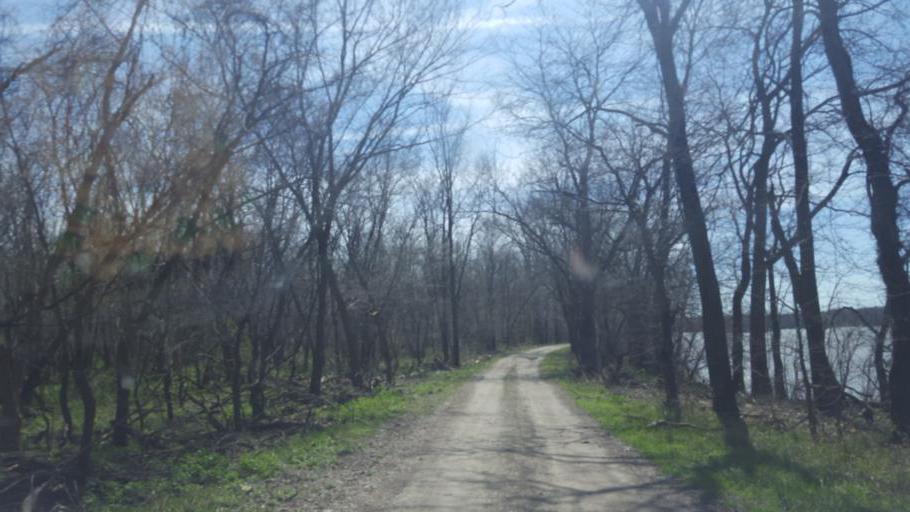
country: US
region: Ohio
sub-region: Delaware County
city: Ashley
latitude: 40.4075
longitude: -83.0458
